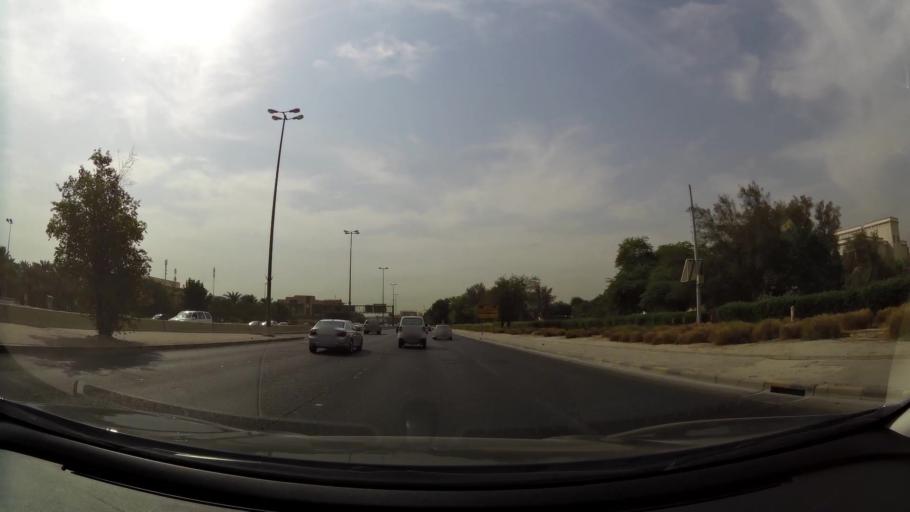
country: KW
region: Al Asimah
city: Ash Shamiyah
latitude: 29.3537
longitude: 47.9731
